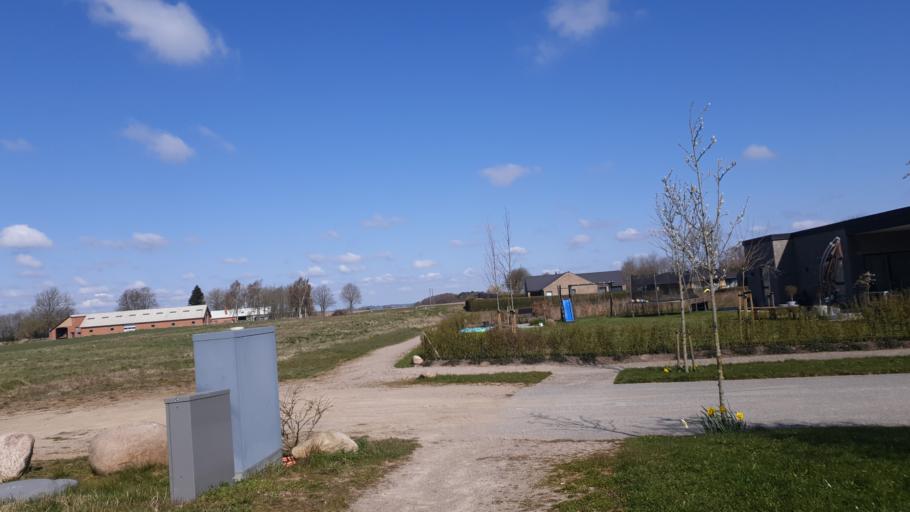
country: DK
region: Central Jutland
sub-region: Hedensted Kommune
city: Hedensted
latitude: 55.8119
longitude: 9.6977
